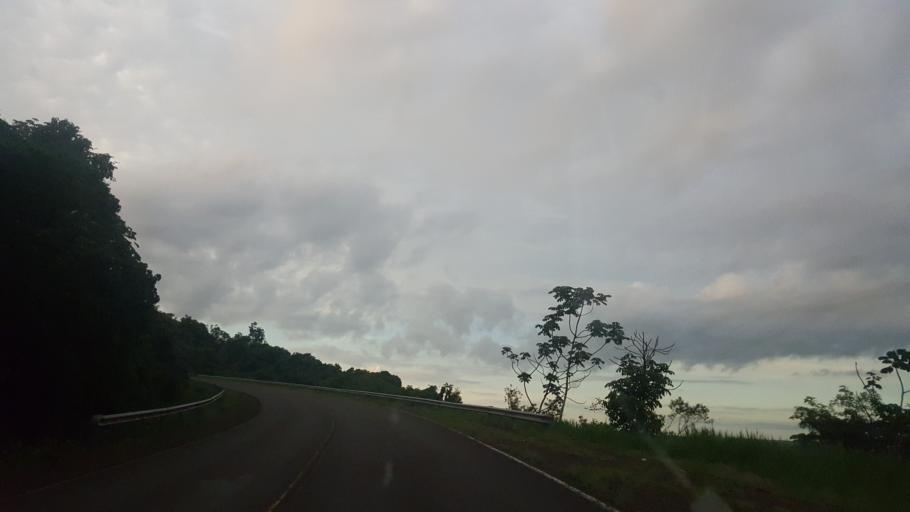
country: AR
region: Misiones
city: Dos de Mayo
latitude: -26.9088
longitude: -54.7413
